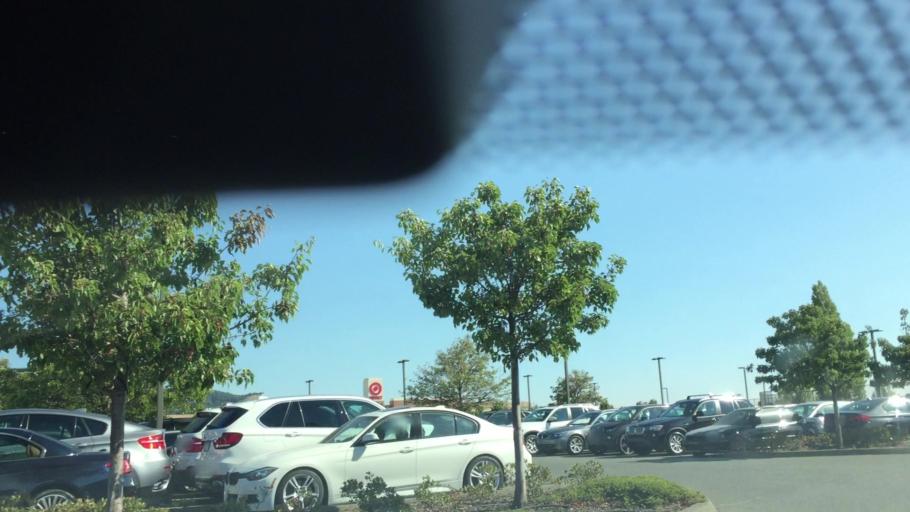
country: US
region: California
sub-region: Marin County
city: San Rafael
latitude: 37.9529
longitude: -122.4913
